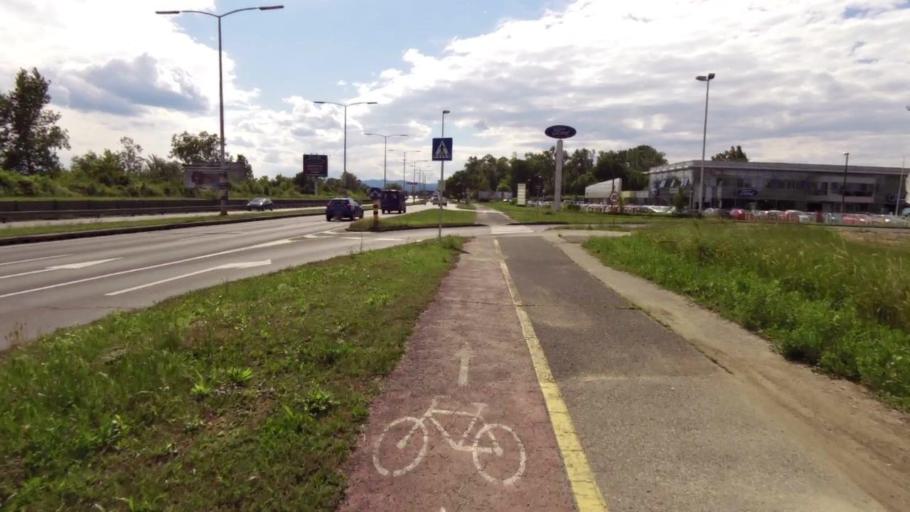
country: HR
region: Grad Zagreb
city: Stenjevec
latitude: 45.7975
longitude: 15.8733
